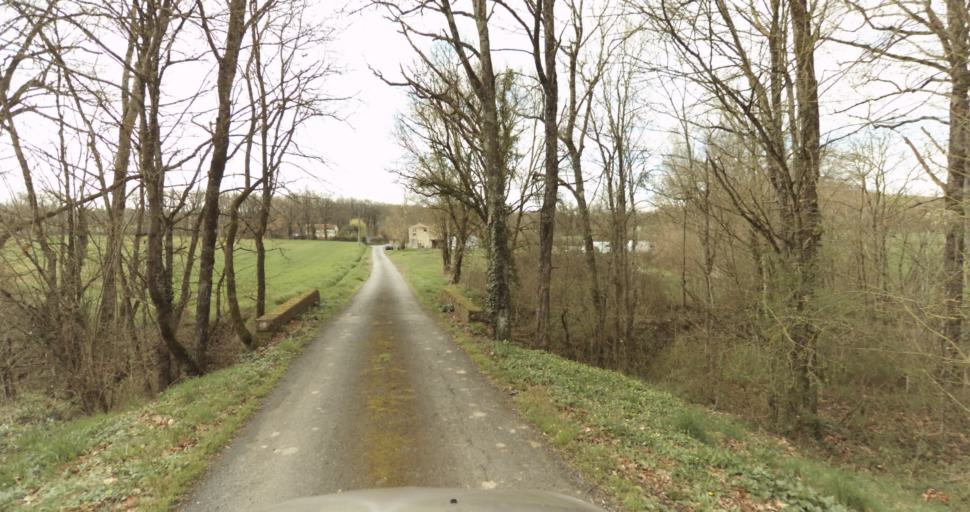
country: FR
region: Midi-Pyrenees
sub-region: Departement du Tarn
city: Frejairolles
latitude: 43.8815
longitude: 2.1987
